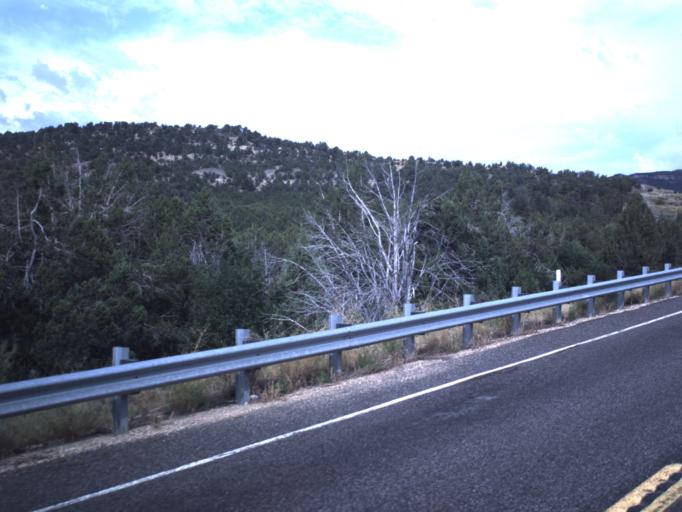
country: US
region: Utah
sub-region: Kane County
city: Kanab
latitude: 37.2568
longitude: -112.7654
